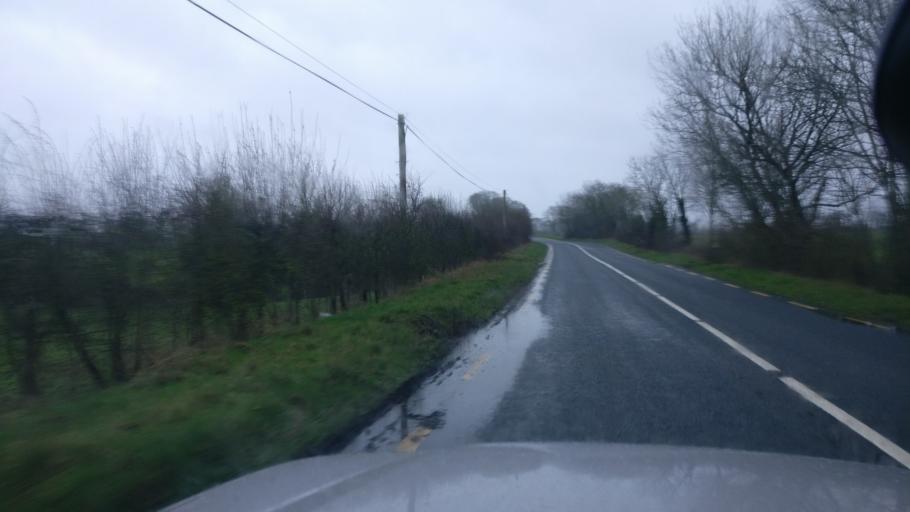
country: IE
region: Connaught
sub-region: County Galway
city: Portumna
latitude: 53.1112
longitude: -8.2207
